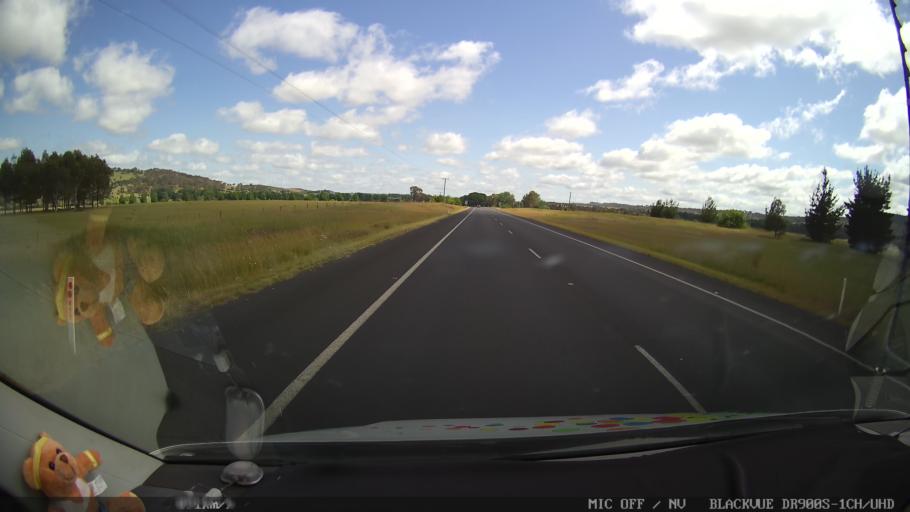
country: AU
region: New South Wales
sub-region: Glen Innes Severn
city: Glen Innes
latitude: -29.8667
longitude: 151.7369
